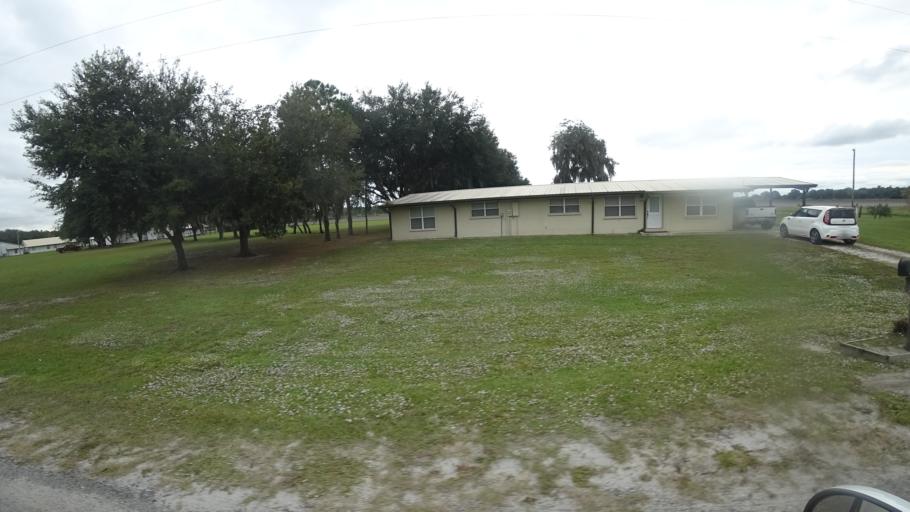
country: US
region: Florida
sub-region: Hillsborough County
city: Wimauma
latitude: 27.5880
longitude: -82.1229
